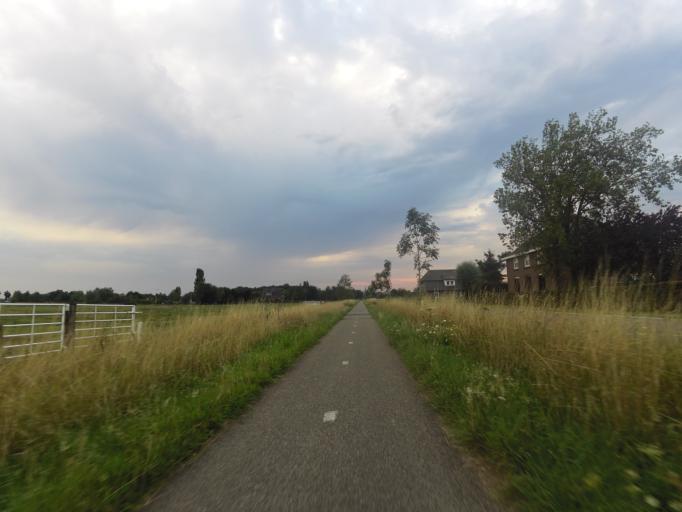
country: NL
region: Gelderland
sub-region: Oude IJsselstreek
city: Gendringen
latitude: 51.9117
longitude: 6.3497
